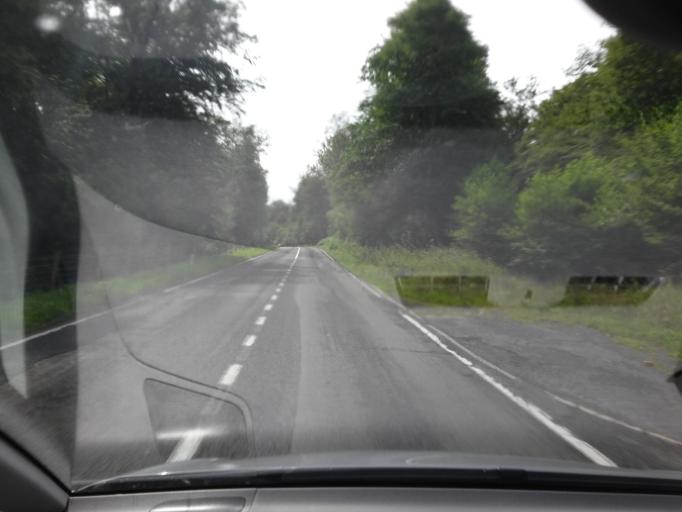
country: BE
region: Wallonia
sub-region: Province du Luxembourg
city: Chiny
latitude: 49.7770
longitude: 5.3496
